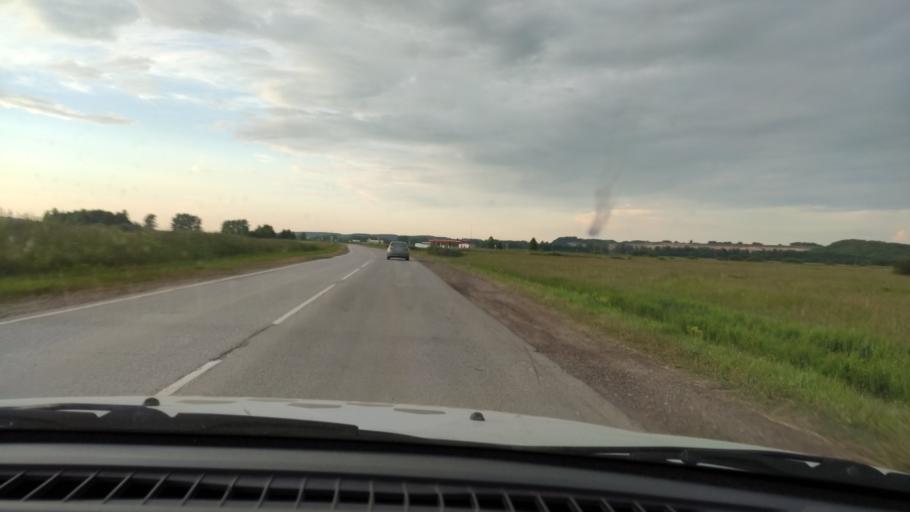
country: RU
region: Perm
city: Kukushtan
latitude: 57.4992
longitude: 56.6463
